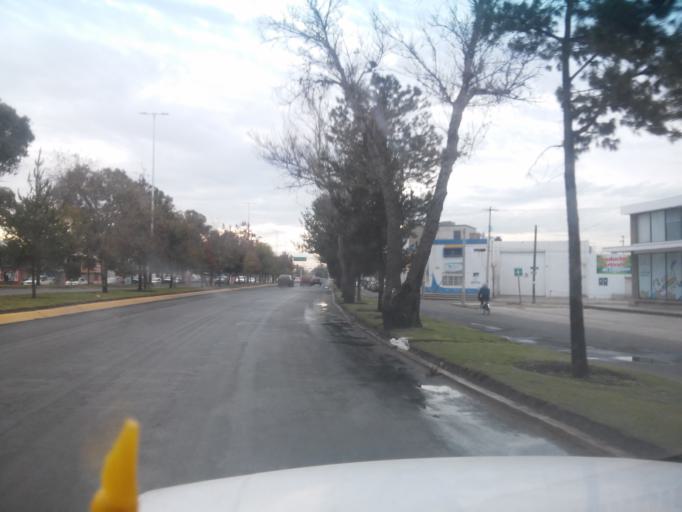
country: MX
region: Durango
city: Victoria de Durango
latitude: 24.0061
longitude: -104.6571
